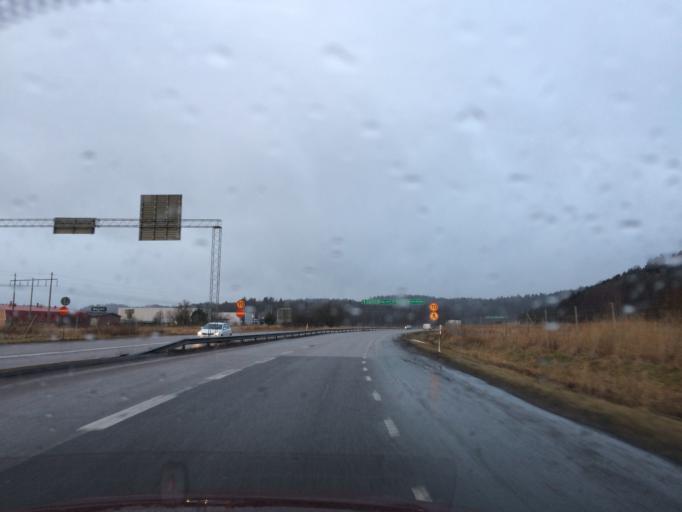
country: SE
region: Halland
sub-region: Kungsbacka Kommun
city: Kungsbacka
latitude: 57.5090
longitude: 12.0629
